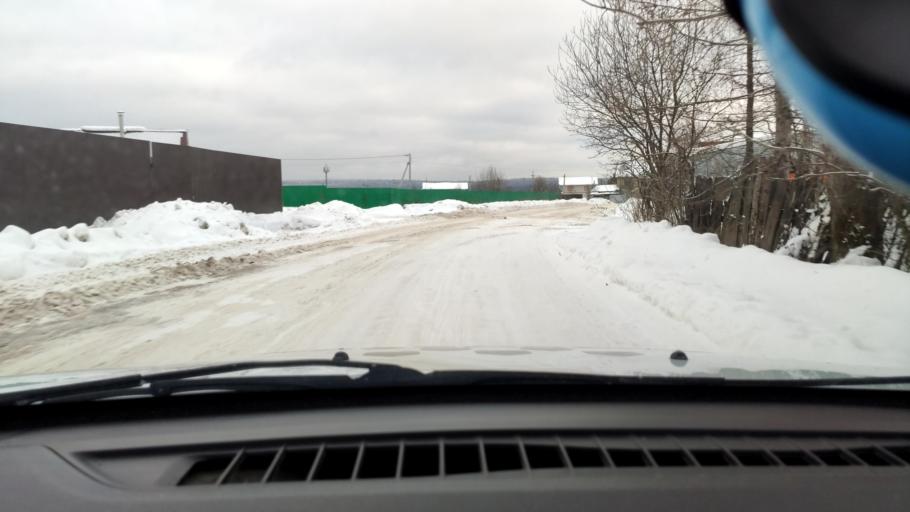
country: RU
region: Perm
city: Overyata
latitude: 58.0808
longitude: 55.9690
